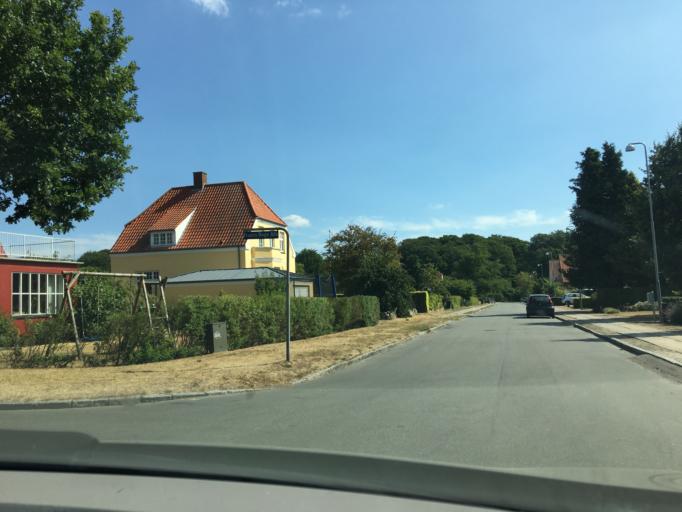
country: DK
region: South Denmark
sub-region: Odense Kommune
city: Odense
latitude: 55.3671
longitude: 10.3763
